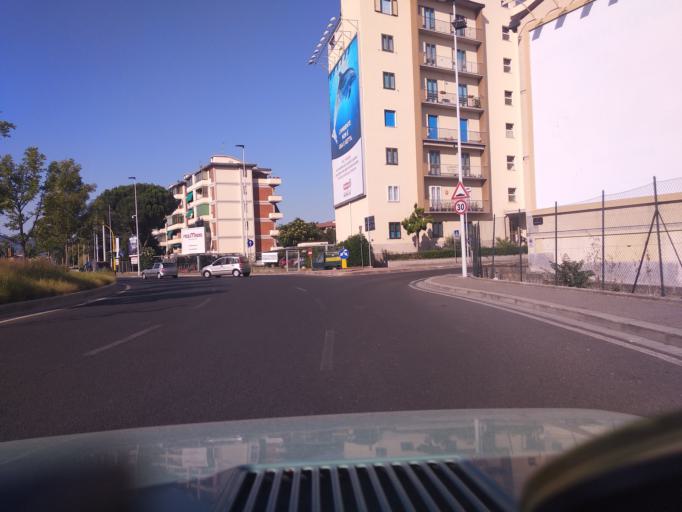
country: IT
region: Tuscany
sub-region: Province of Florence
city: Scandicci
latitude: 43.7672
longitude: 11.2092
